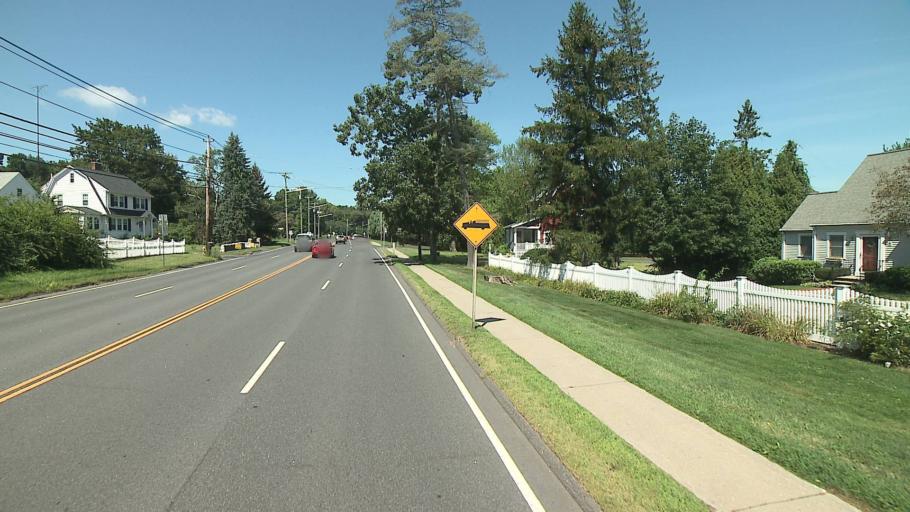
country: US
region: Connecticut
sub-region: Fairfield County
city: Trumbull
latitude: 41.2429
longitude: -73.1920
